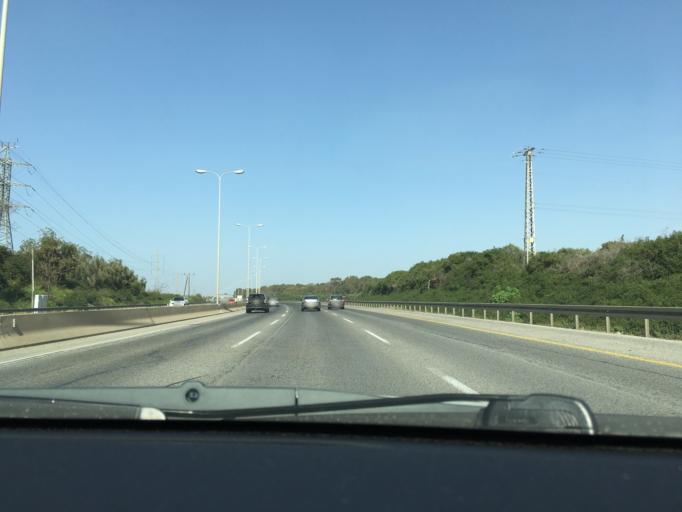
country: IL
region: Central District
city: Hod HaSharon
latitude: 32.1448
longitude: 34.8738
